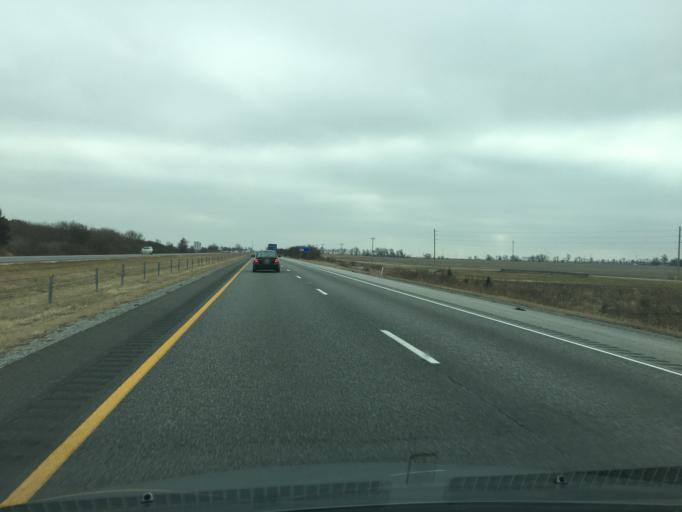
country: US
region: Indiana
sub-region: Jasper County
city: Remington
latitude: 40.7963
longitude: -87.1405
